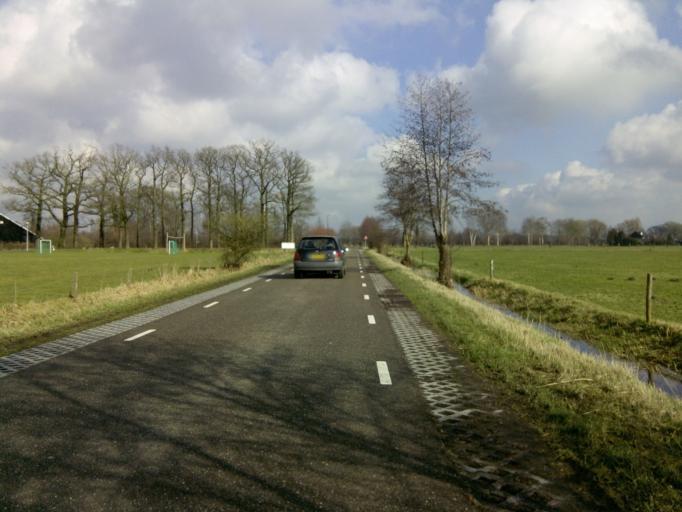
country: NL
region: Utrecht
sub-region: Gemeente Woudenberg
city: Woudenberg
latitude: 52.0649
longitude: 5.4257
